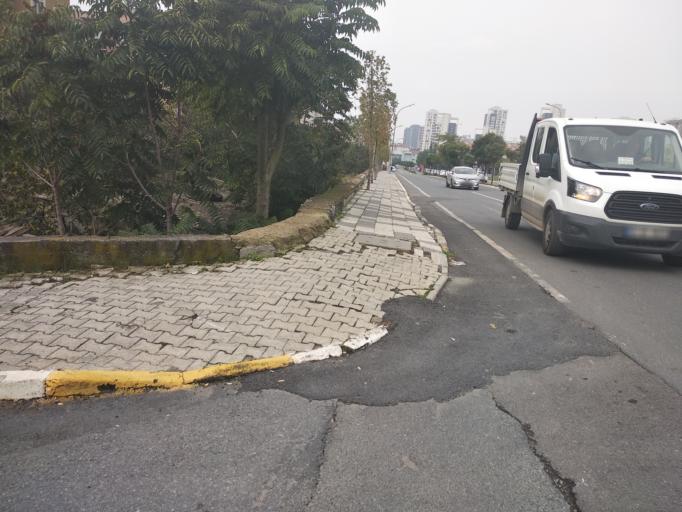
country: TR
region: Istanbul
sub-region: Atasehir
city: Atasehir
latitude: 40.9824
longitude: 29.1278
